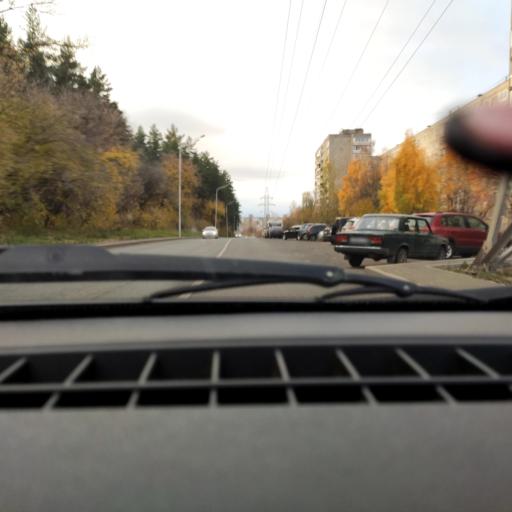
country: RU
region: Bashkortostan
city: Ufa
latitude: 54.7072
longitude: 56.0086
